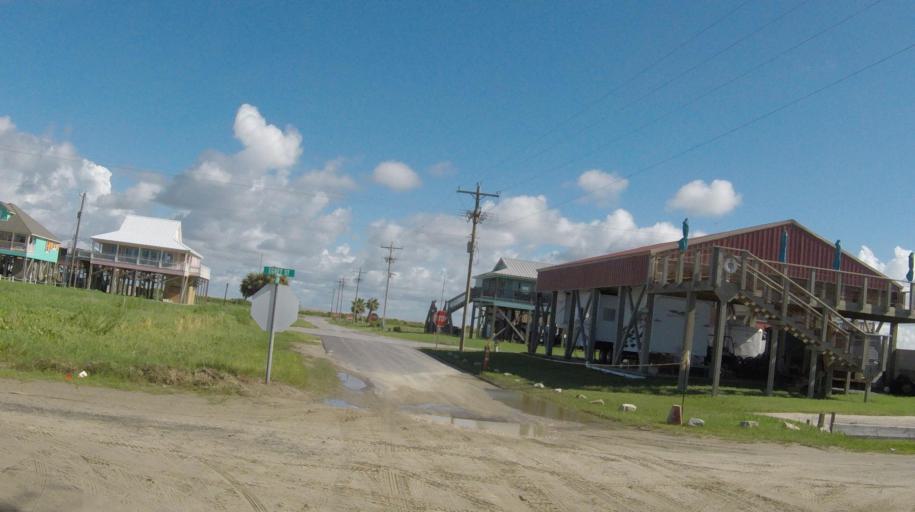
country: US
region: Louisiana
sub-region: Cameron Parish
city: Cameron
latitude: 29.7700
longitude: -93.4516
